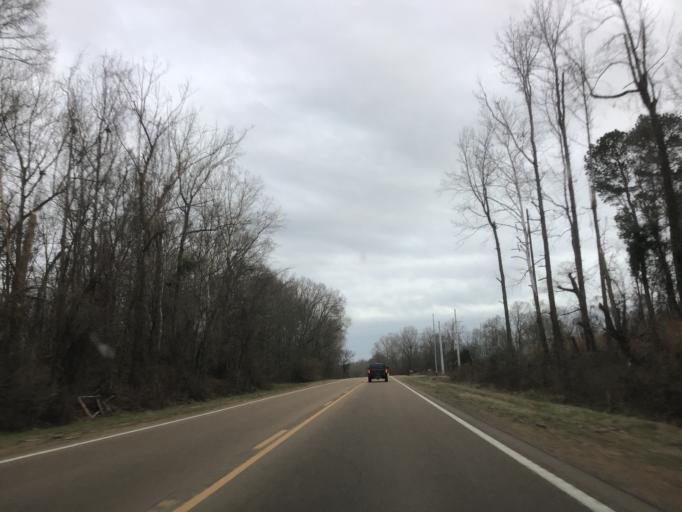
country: US
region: Mississippi
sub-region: Warren County
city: Beechwood
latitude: 32.3144
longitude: -90.8098
